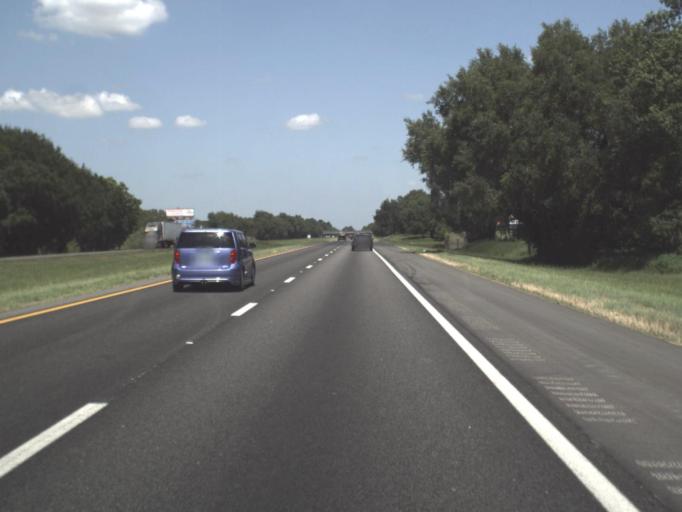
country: US
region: Florida
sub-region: Madison County
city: Madison
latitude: 30.3999
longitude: -83.3767
